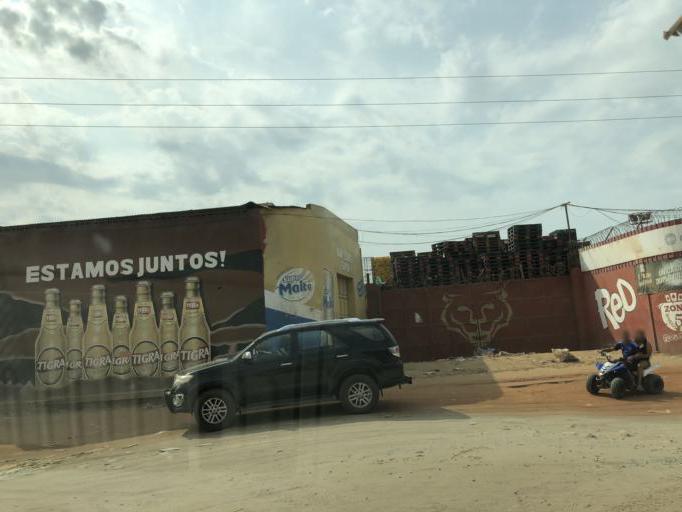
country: AO
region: Luanda
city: Luanda
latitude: -8.8963
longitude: 13.3517
